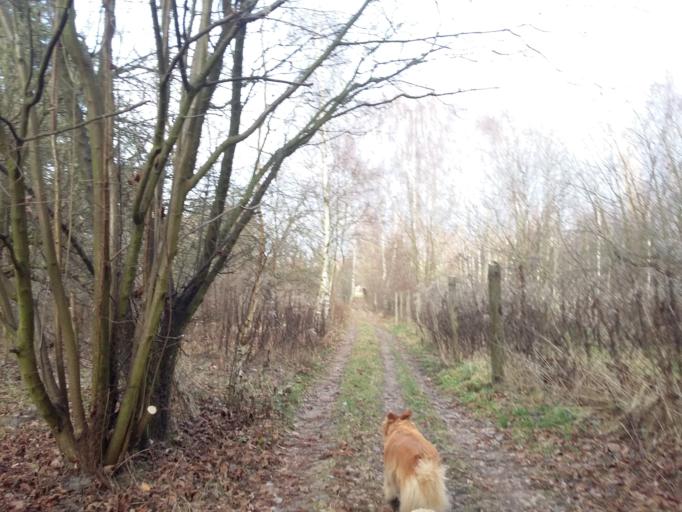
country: PL
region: Lodz Voivodeship
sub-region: Powiat pabianicki
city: Ksawerow
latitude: 51.7355
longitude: 19.4117
